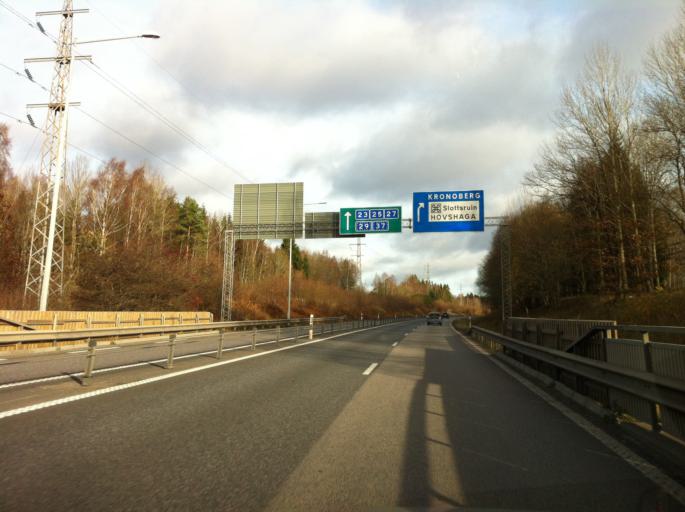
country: SE
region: Kronoberg
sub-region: Vaxjo Kommun
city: Gemla
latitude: 56.8273
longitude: 14.6919
